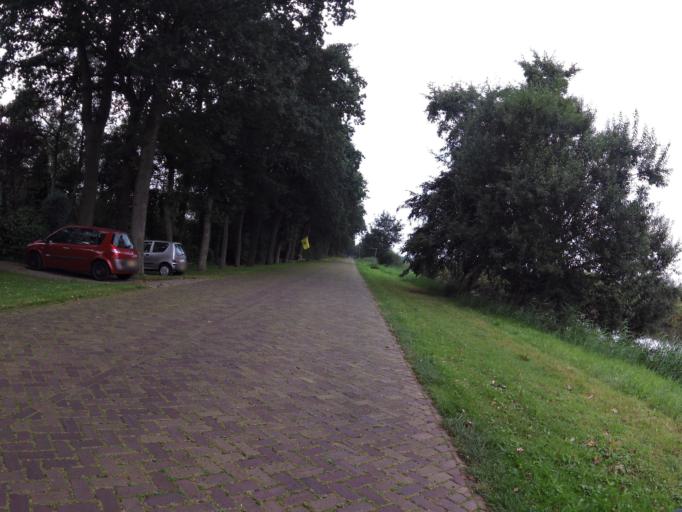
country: NL
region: Drenthe
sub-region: Gemeente Emmen
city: Schoonebeek
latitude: 52.6822
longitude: 6.9335
